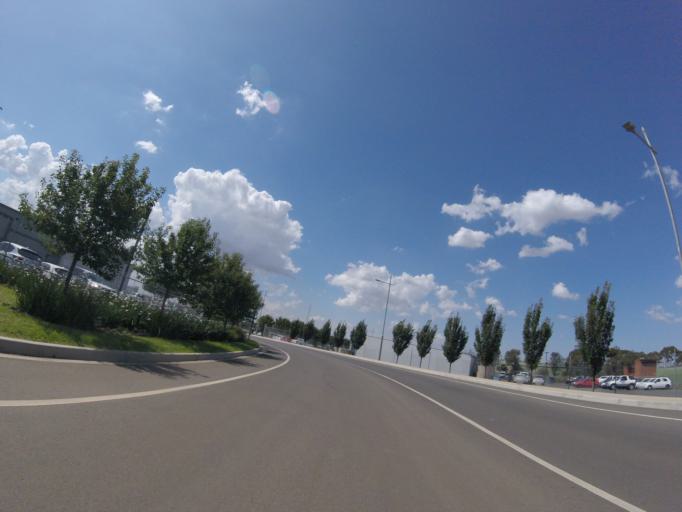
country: AU
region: Victoria
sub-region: Moreland
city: Oak Park
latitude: -37.7228
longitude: 144.9025
